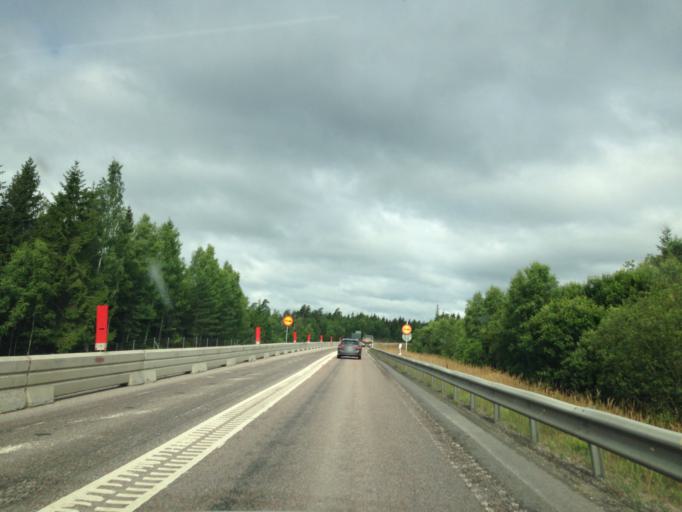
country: SE
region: Stockholm
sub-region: Varmdo Kommun
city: Gustavsberg
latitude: 59.3143
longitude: 18.3589
